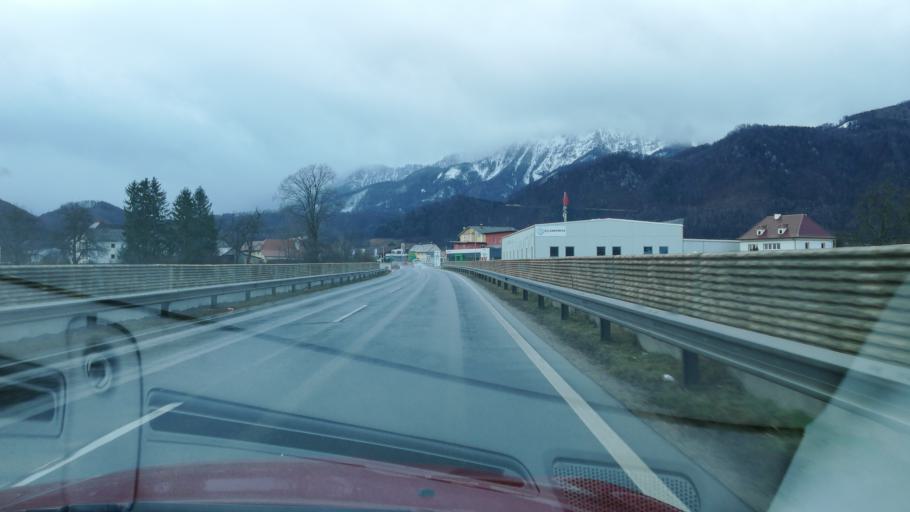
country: AT
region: Upper Austria
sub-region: Politischer Bezirk Kirchdorf an der Krems
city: Micheldorf in Oberoesterreich
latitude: 47.8856
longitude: 14.1278
